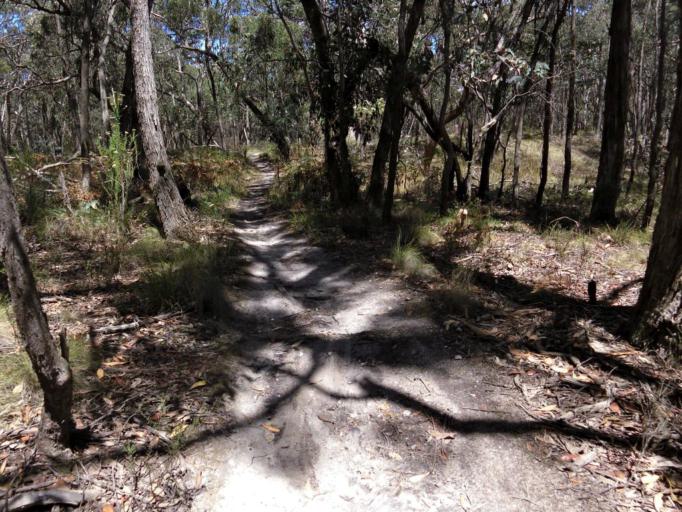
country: AU
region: Victoria
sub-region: Melton
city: Melton West
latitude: -37.4975
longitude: 144.5500
